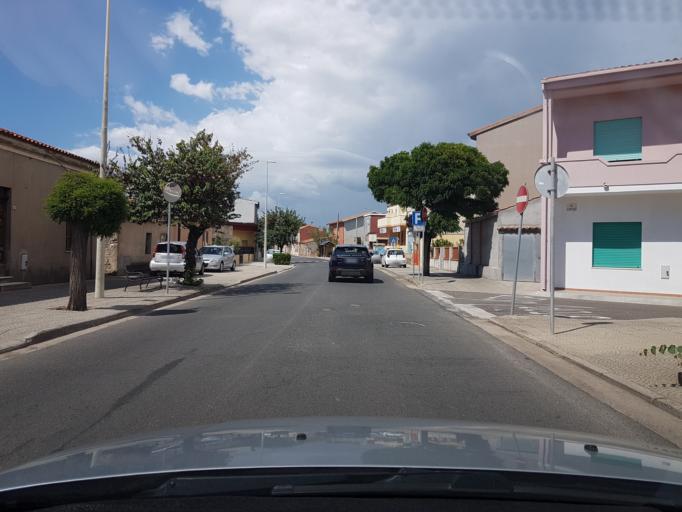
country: IT
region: Sardinia
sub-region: Provincia di Oristano
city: Riola Sardo
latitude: 39.9923
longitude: 8.5417
